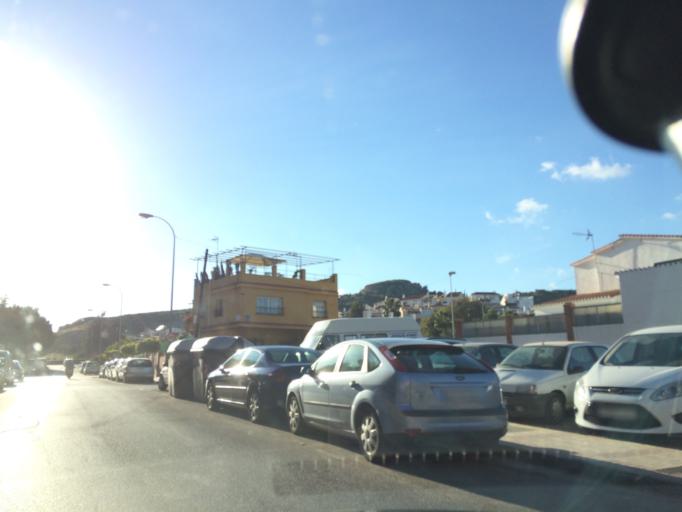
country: ES
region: Andalusia
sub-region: Provincia de Malaga
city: Malaga
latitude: 36.7264
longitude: -4.4490
